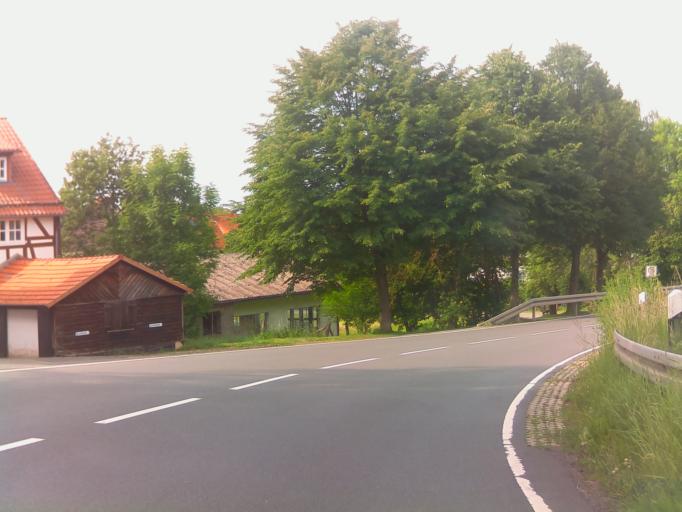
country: DE
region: Hesse
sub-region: Regierungsbezirk Kassel
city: Sachsenhausen
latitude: 51.2803
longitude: 9.0683
